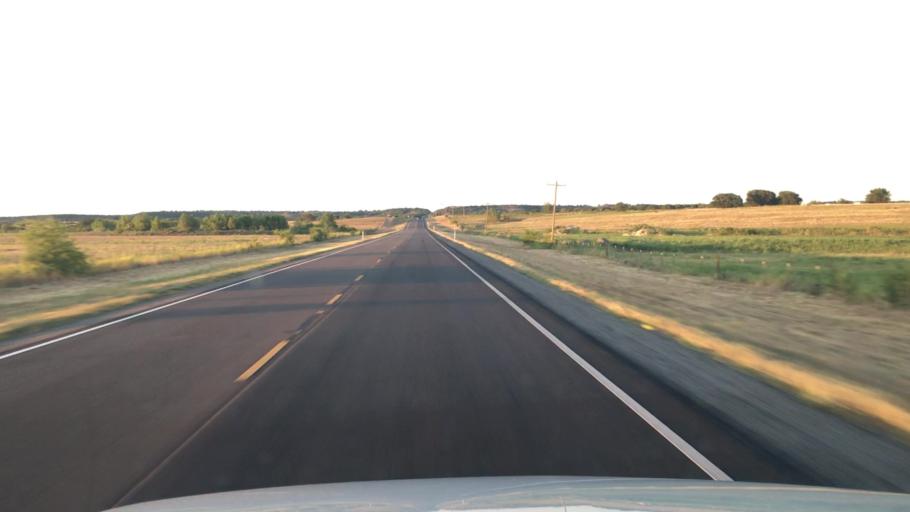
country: US
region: Texas
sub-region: Hamilton County
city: Hico
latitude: 32.0774
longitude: -97.9822
